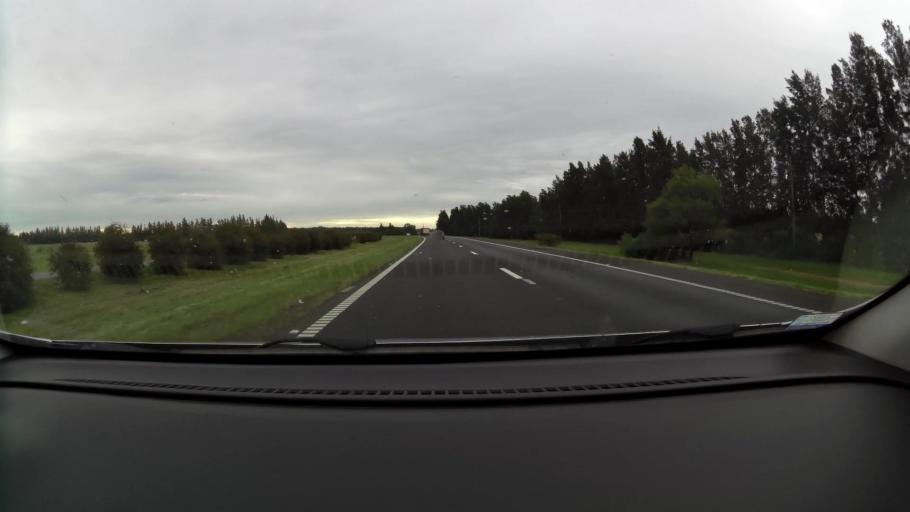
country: AR
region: Buenos Aires
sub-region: Partido de San Pedro
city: San Pedro
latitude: -33.7098
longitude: -59.8314
